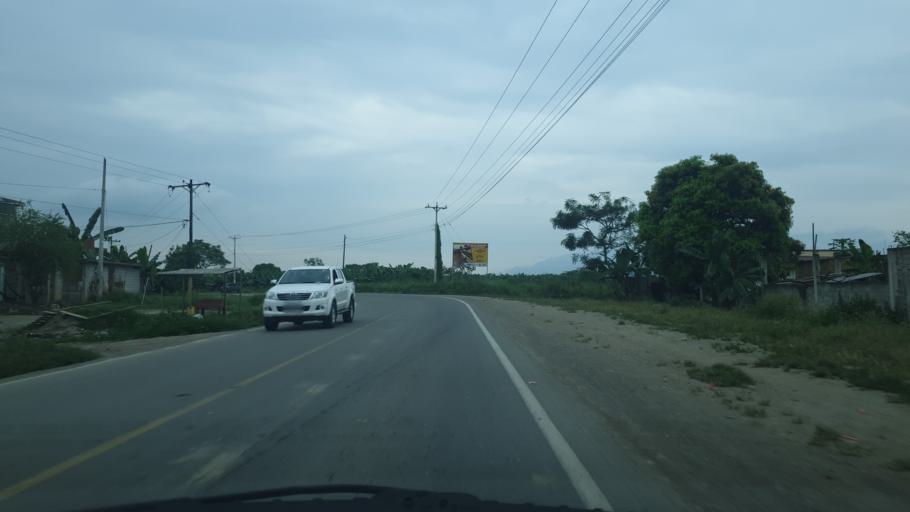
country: EC
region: El Oro
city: Pasaje
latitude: -3.3468
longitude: -79.8138
